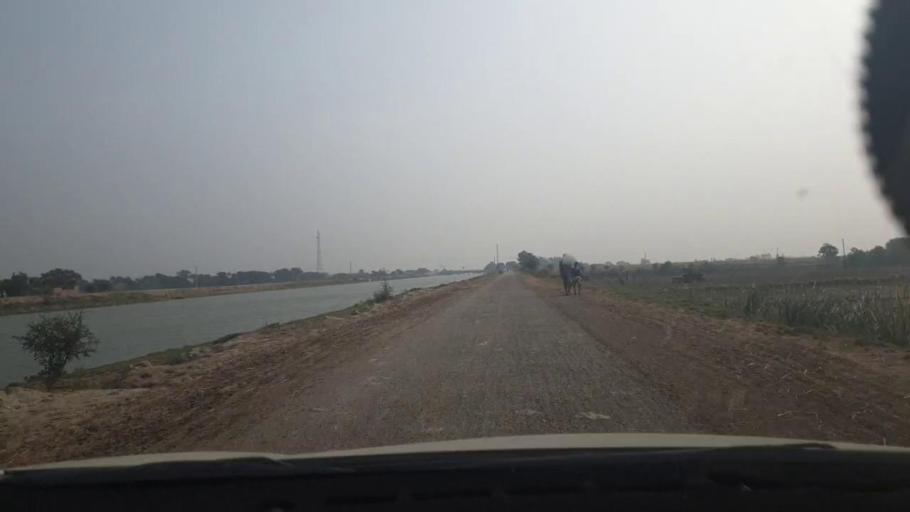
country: PK
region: Sindh
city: Tando Muhammad Khan
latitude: 24.9655
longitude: 68.4950
